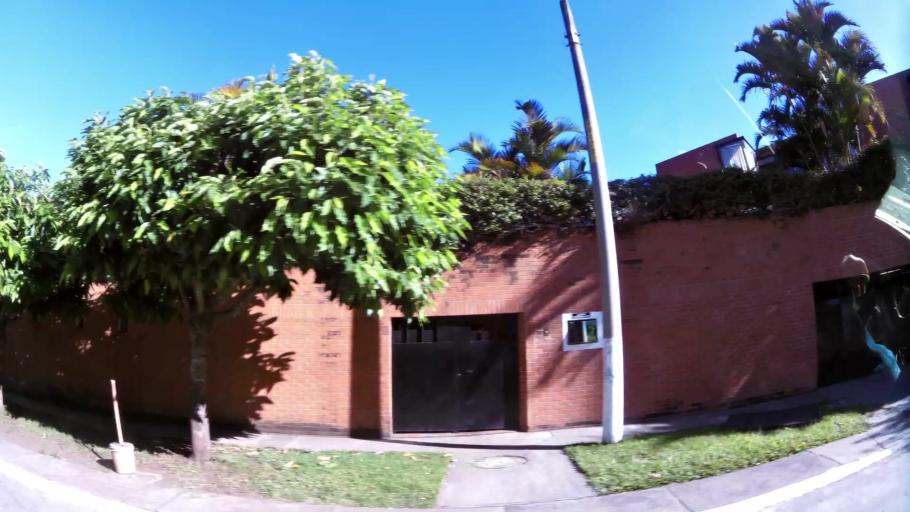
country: GT
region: Guatemala
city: Santa Catarina Pinula
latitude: 14.5657
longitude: -90.5252
